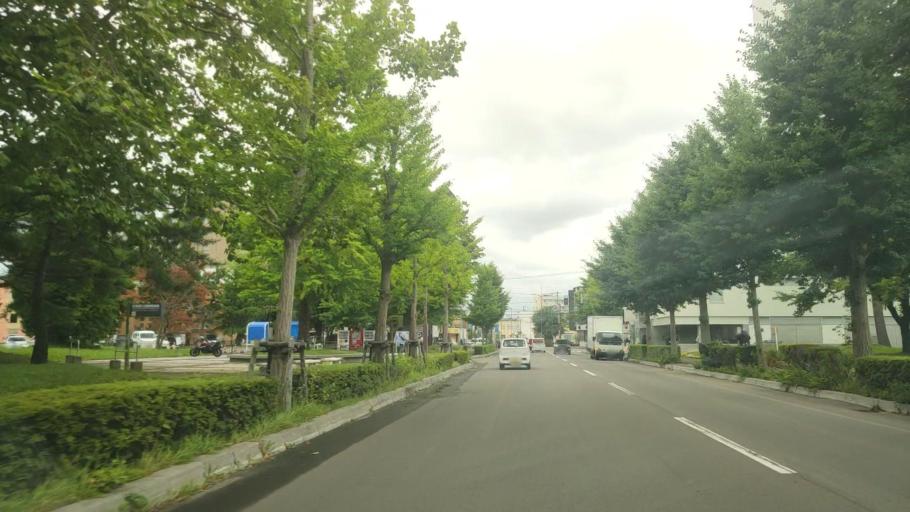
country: JP
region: Hokkaido
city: Hakodate
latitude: 41.7941
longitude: 140.7546
